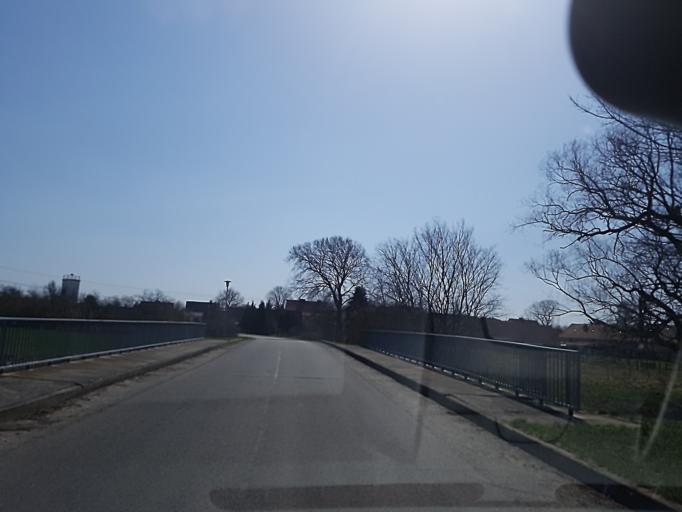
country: DE
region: Brandenburg
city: Schonborn
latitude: 51.5620
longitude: 13.4818
